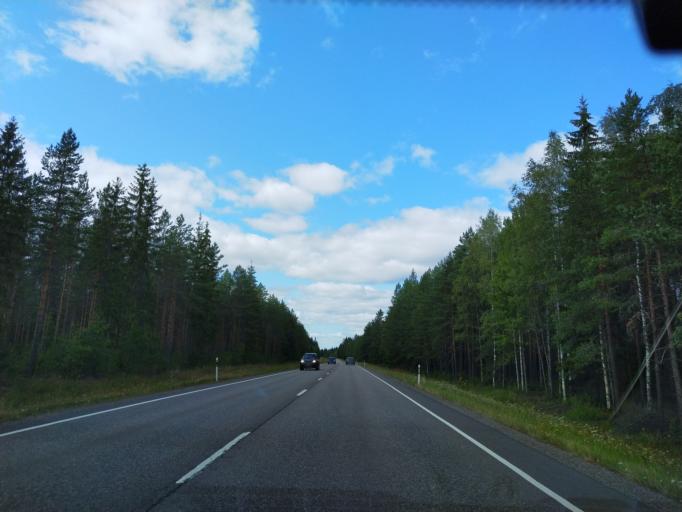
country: FI
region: Haeme
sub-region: Haemeenlinna
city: Renko
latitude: 60.7632
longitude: 24.2726
